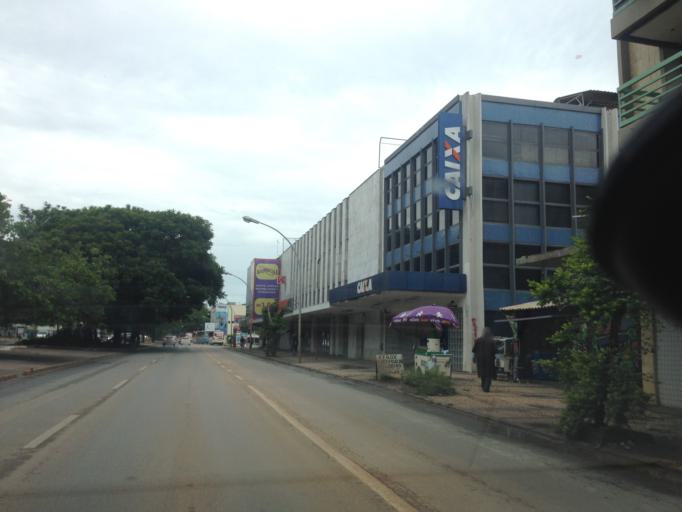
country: BR
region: Federal District
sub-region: Brasilia
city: Brasilia
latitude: -15.8051
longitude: -47.8976
